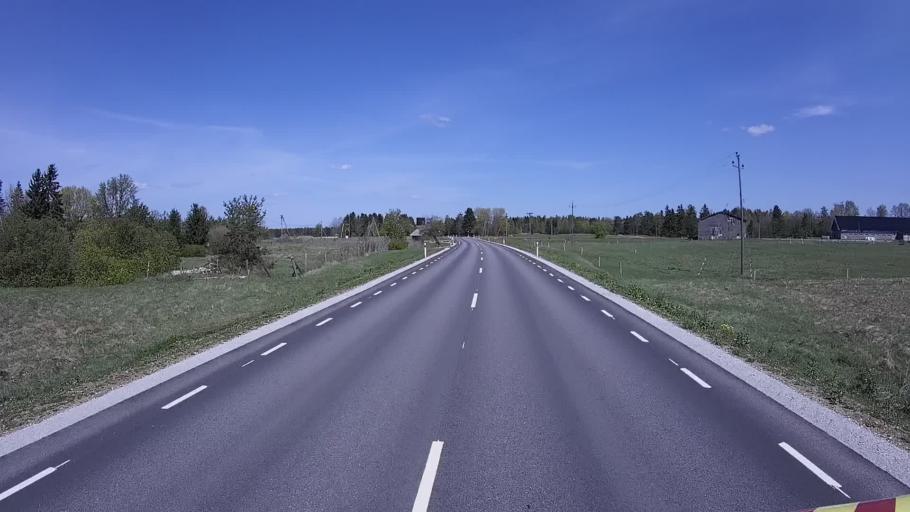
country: EE
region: Harju
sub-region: Nissi vald
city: Turba
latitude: 59.1810
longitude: 24.0844
